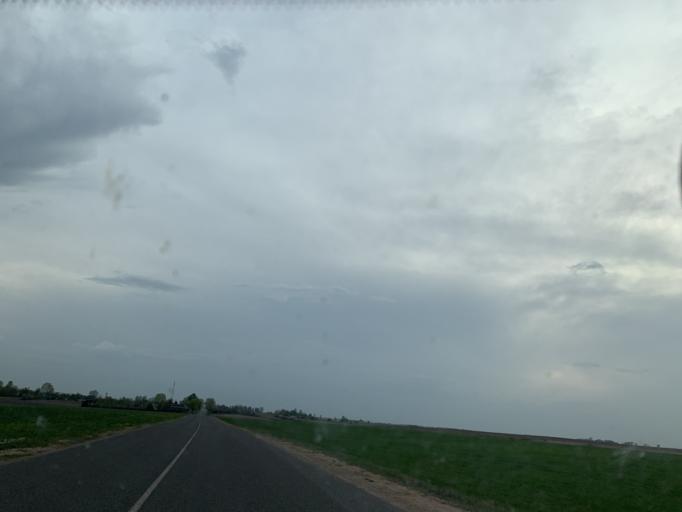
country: BY
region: Minsk
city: Kapyl'
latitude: 53.2889
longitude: 26.9895
